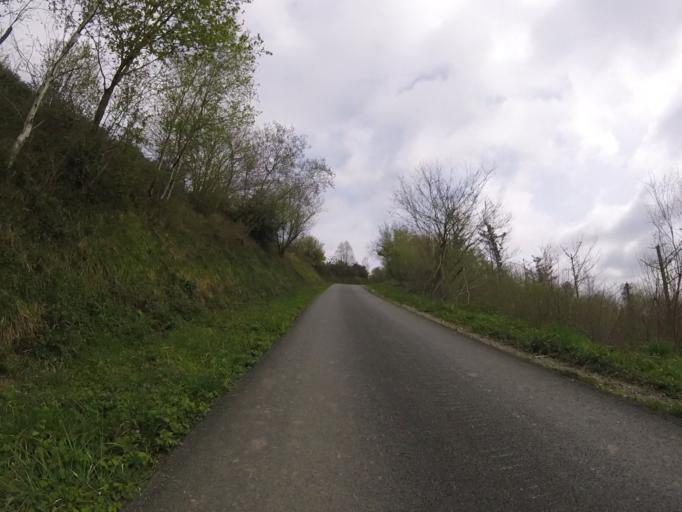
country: ES
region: Basque Country
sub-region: Provincia de Guipuzcoa
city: Asteasu
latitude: 43.2262
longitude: -2.0948
